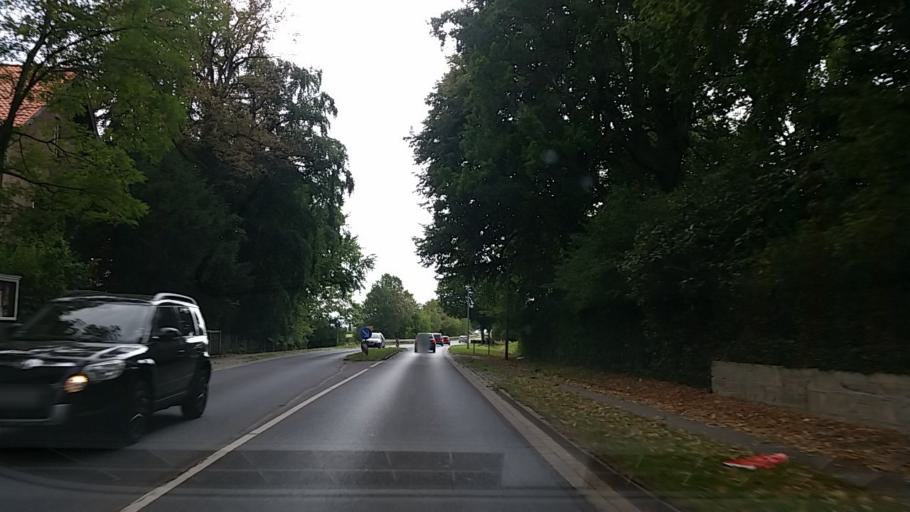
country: DE
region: Lower Saxony
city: Ohrum
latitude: 52.1399
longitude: 10.5496
